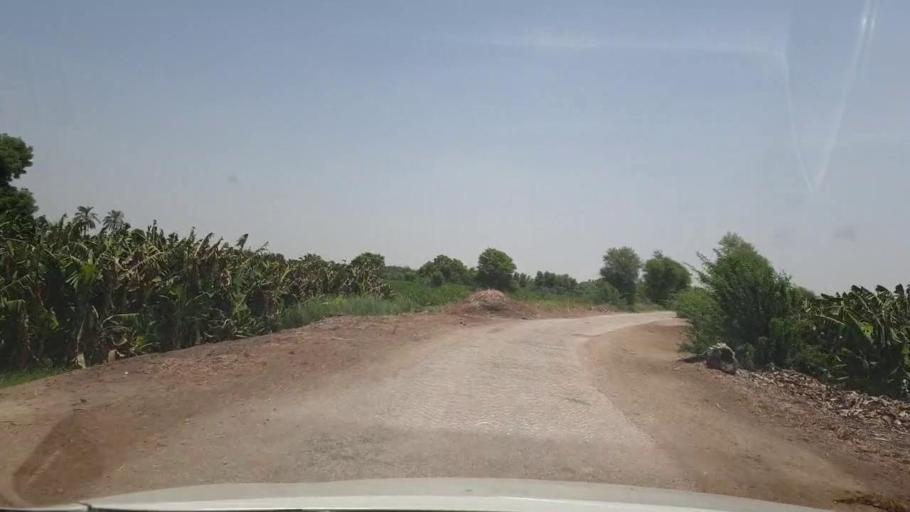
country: PK
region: Sindh
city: Bozdar
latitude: 27.2044
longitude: 68.6707
